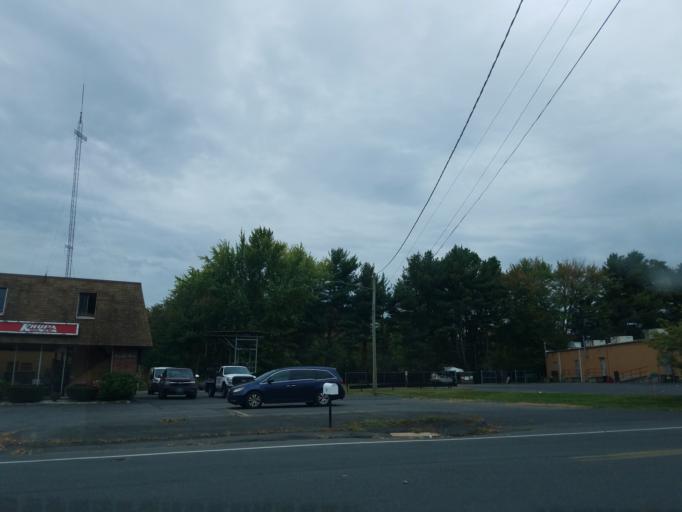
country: US
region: Connecticut
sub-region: Hartford County
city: Thompsonville
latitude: 41.9972
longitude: -72.6130
